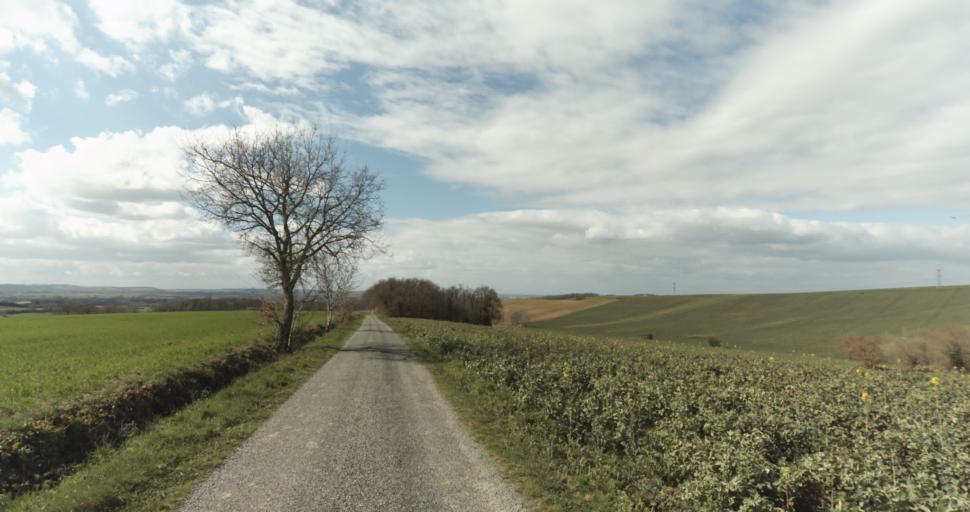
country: FR
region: Midi-Pyrenees
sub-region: Departement de la Haute-Garonne
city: Auterive
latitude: 43.3841
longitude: 1.4839
